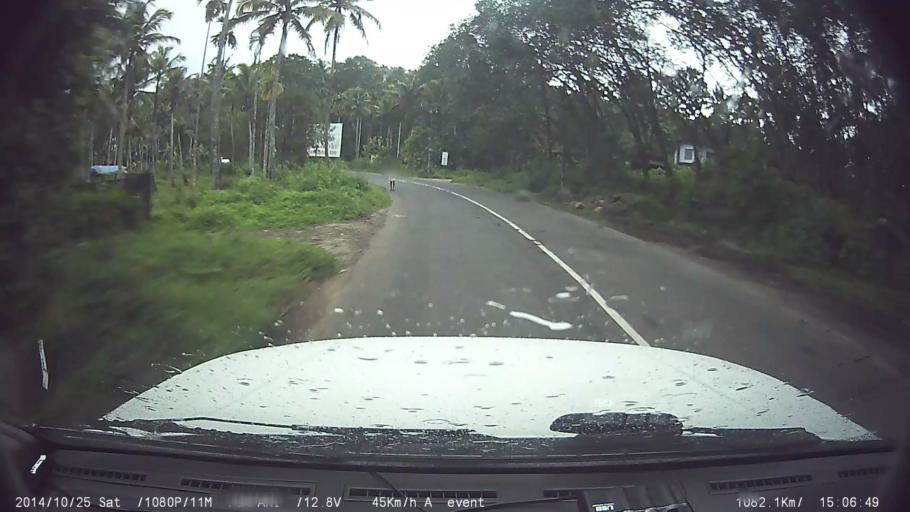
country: IN
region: Kerala
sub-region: Kottayam
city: Palackattumala
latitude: 9.8295
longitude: 76.5920
